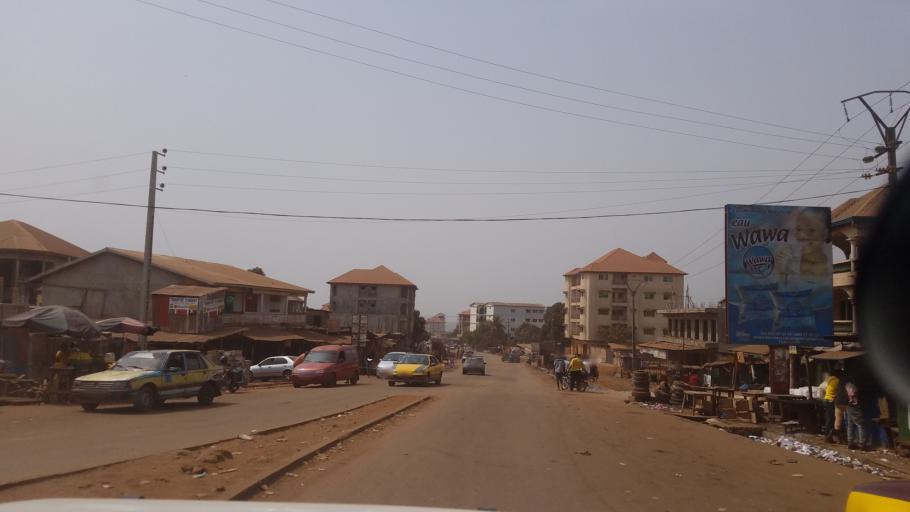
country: GN
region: Kindia
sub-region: Prefecture de Dubreka
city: Dubreka
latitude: 9.6695
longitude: -13.5583
